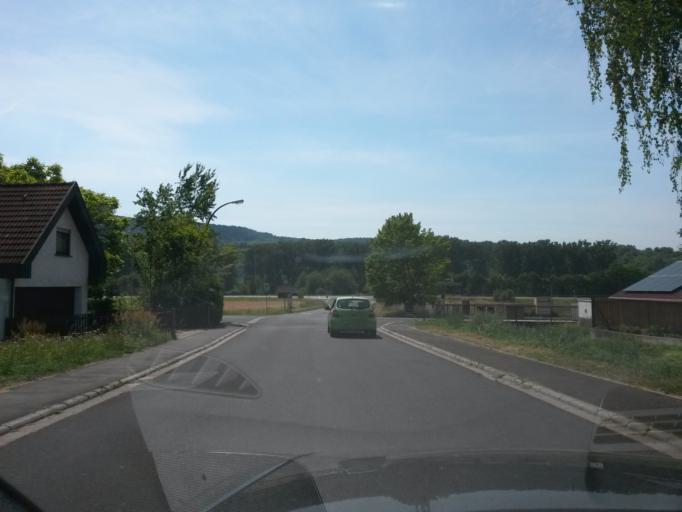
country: DE
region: Bavaria
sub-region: Regierungsbezirk Unterfranken
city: Thungersheim
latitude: 49.8753
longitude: 9.8445
